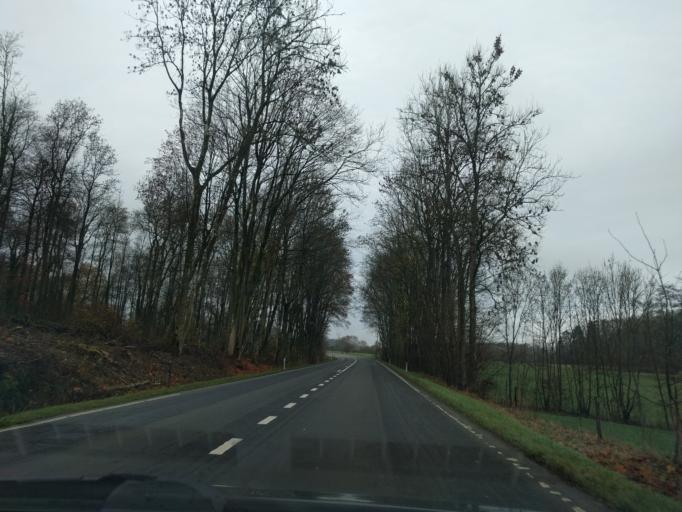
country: BE
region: Wallonia
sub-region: Province de Namur
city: Mettet
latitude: 50.2380
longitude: 4.7056
